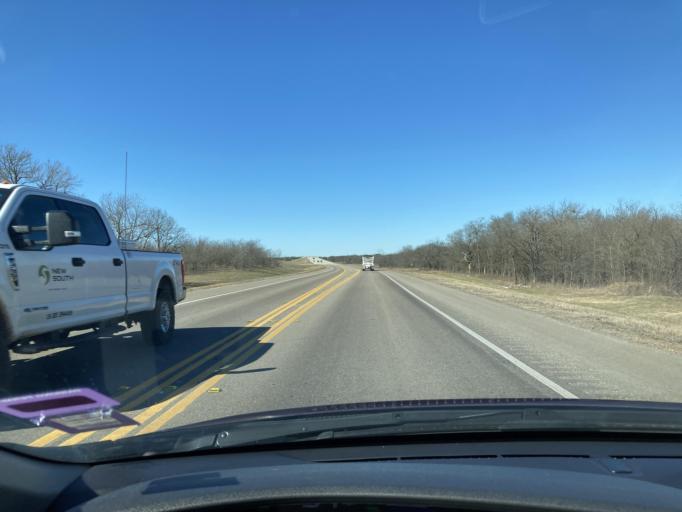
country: US
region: Texas
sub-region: Navarro County
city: Corsicana
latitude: 32.0428
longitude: -96.4630
